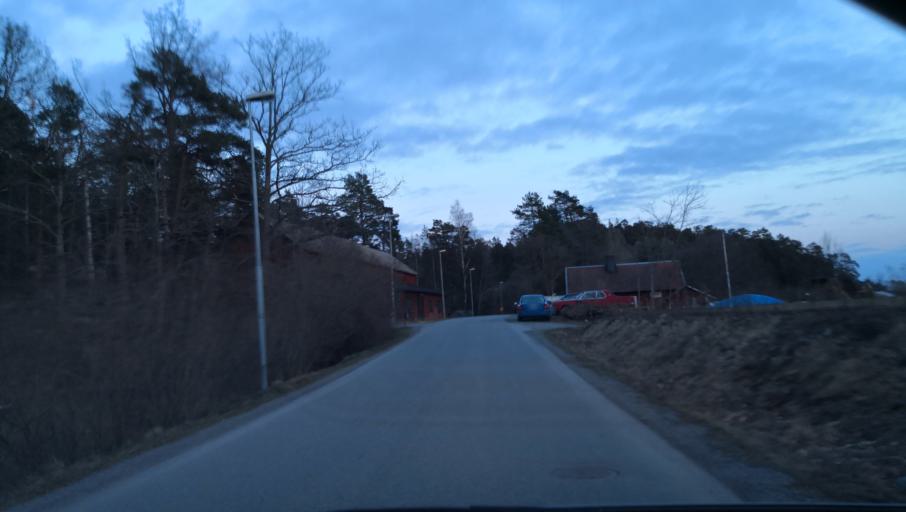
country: SE
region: Stockholm
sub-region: Nacka Kommun
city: Boo
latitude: 59.3312
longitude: 18.3156
